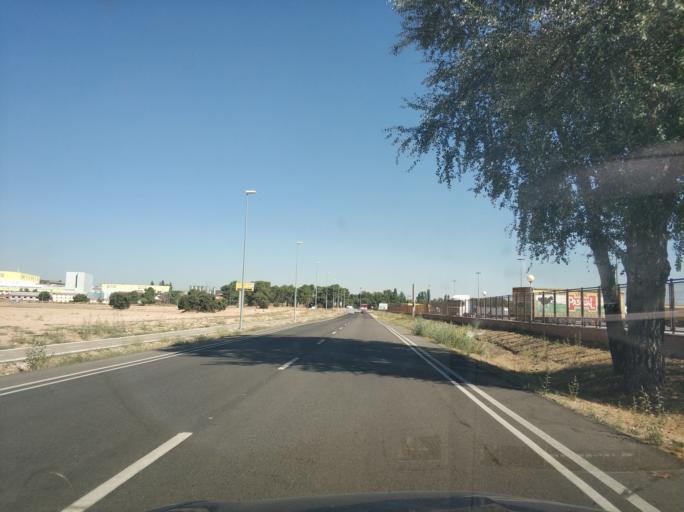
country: ES
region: Castille and Leon
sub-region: Provincia de Burgos
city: Aranda de Duero
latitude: 41.6696
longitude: -3.7006
